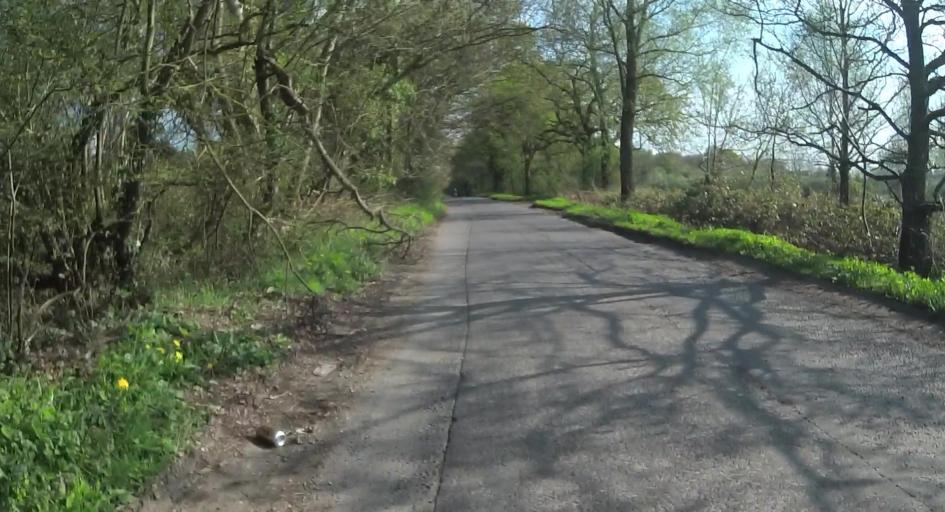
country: GB
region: England
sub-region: West Berkshire
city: Stratfield Mortimer
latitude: 51.3426
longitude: -1.0679
